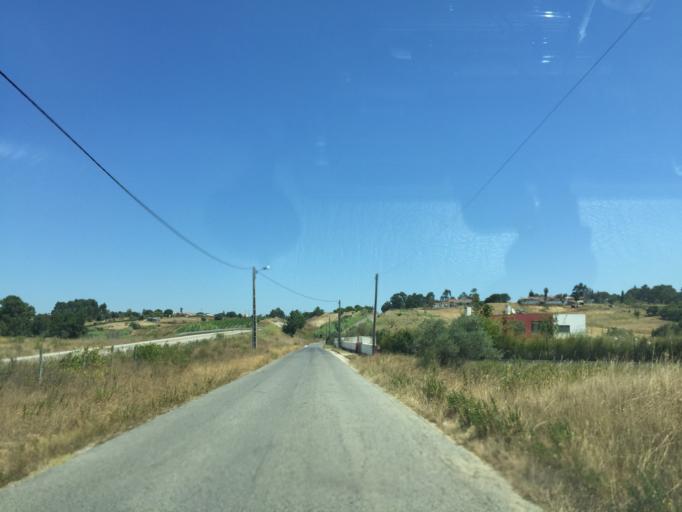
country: PT
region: Lisbon
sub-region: Azambuja
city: Aveiras de Cima
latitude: 39.1502
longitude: -8.8916
